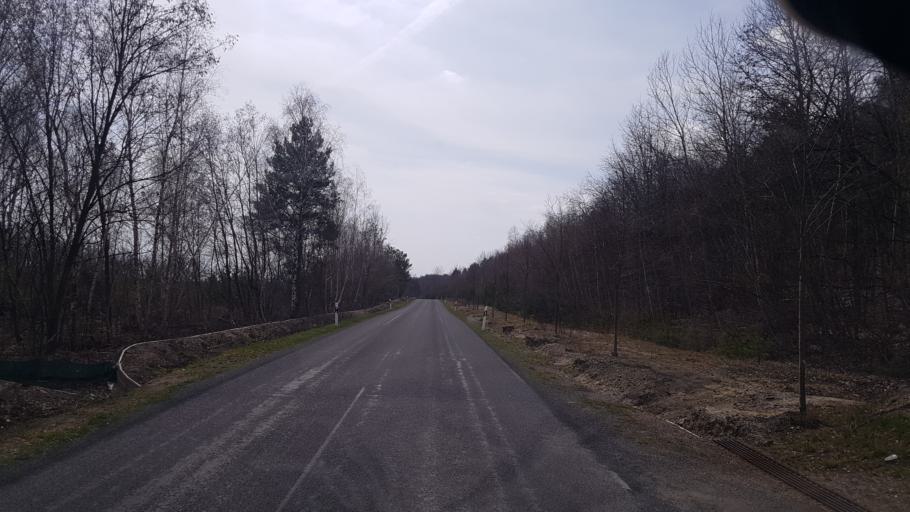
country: DE
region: Brandenburg
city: Schipkau
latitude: 51.5308
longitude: 13.8452
